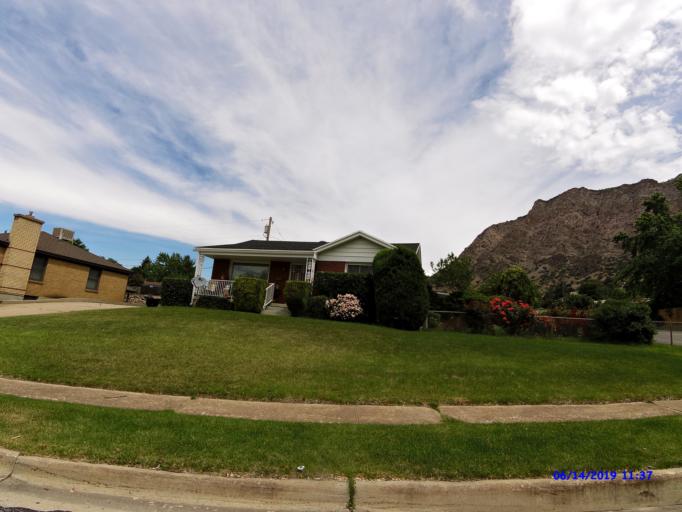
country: US
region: Utah
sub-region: Weber County
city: Ogden
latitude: 41.2524
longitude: -111.9391
